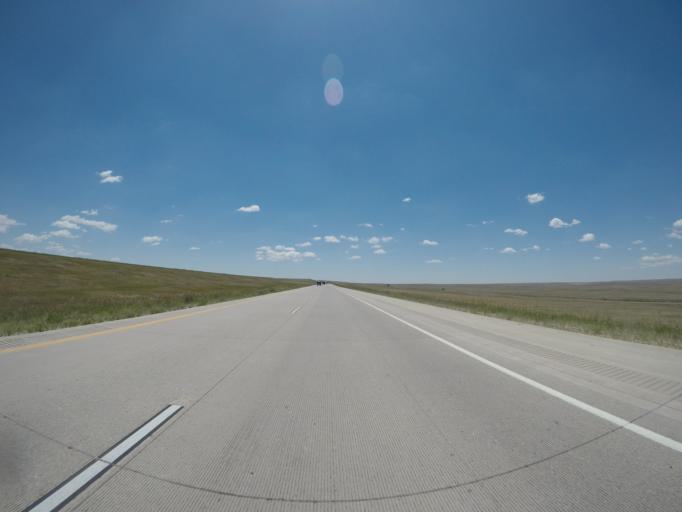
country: US
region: Colorado
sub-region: Lincoln County
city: Limon
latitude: 39.3794
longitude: -103.8879
